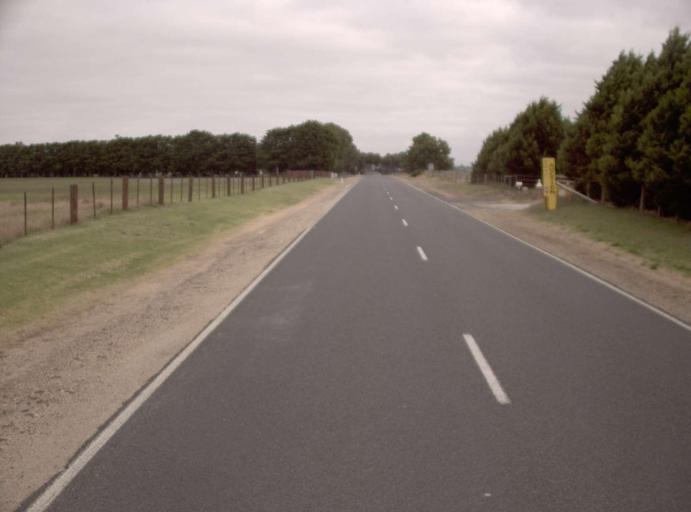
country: AU
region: Victoria
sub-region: Wellington
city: Sale
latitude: -38.0967
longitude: 146.9876
